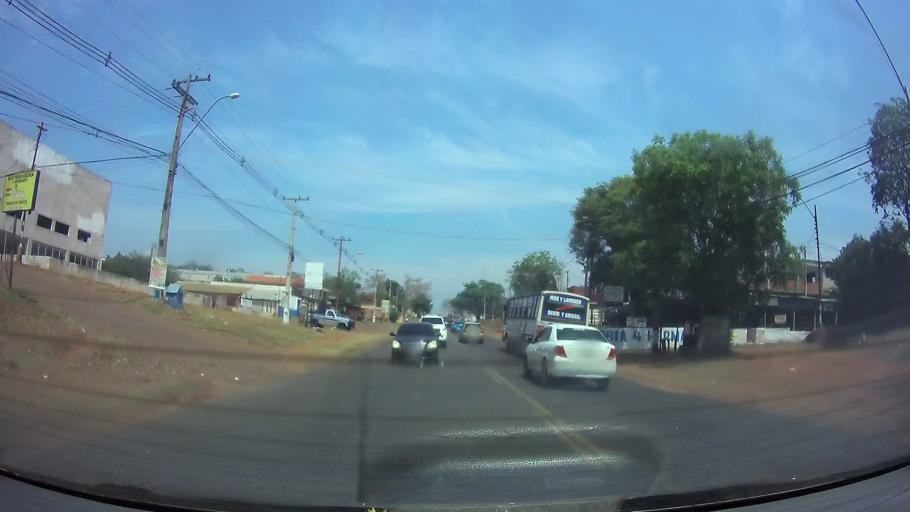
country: PY
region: Central
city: Capiata
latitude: -25.3963
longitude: -57.4666
